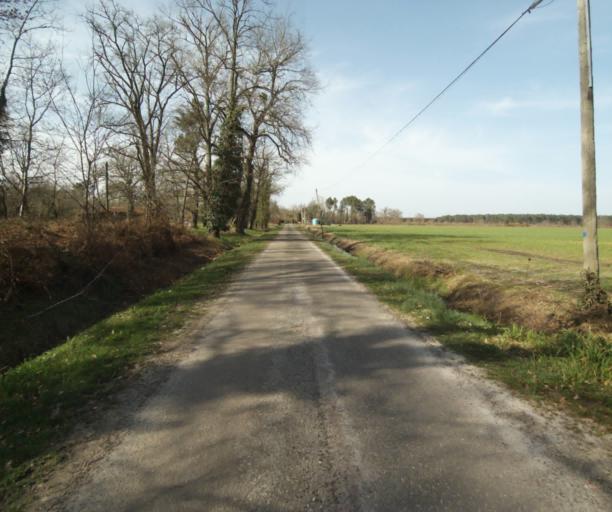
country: FR
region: Aquitaine
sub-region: Departement des Landes
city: Roquefort
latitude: 44.1587
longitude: -0.2009
